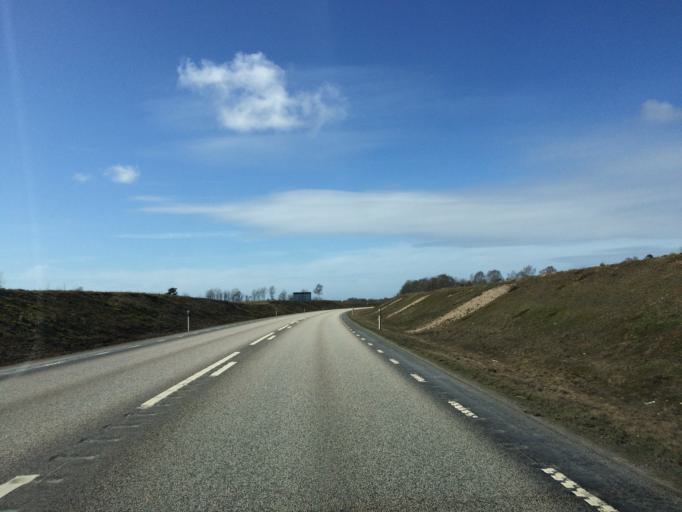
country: SE
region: Halland
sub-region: Laholms Kommun
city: Veinge
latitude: 56.5262
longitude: 13.1828
